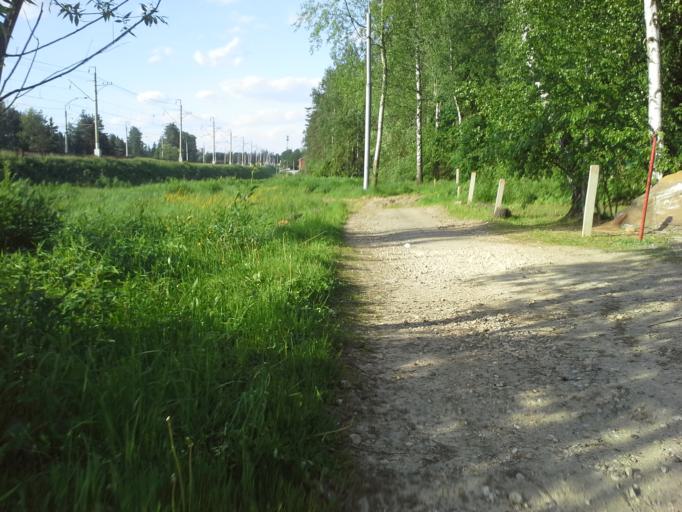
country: RU
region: Moscow
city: Tolstopal'tsevo
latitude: 55.6202
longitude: 37.2114
